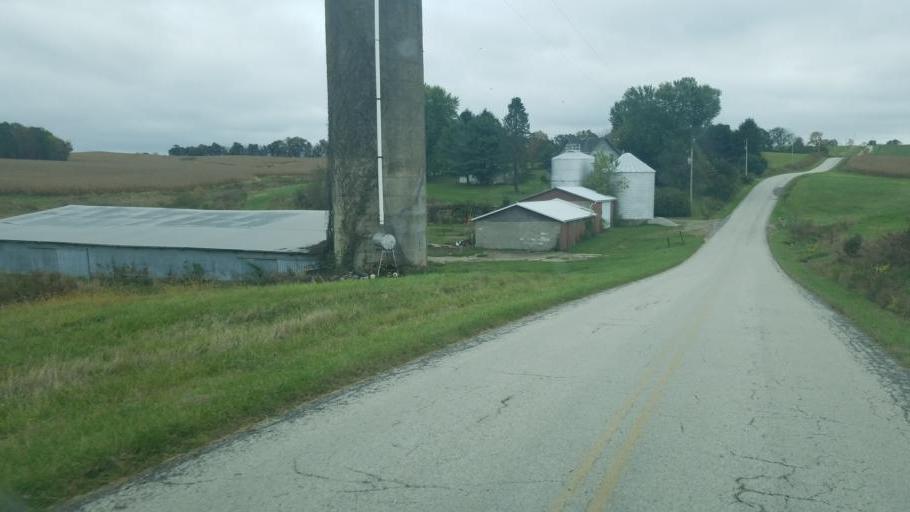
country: US
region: Ohio
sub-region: Ashland County
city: Loudonville
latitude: 40.5697
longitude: -82.1645
